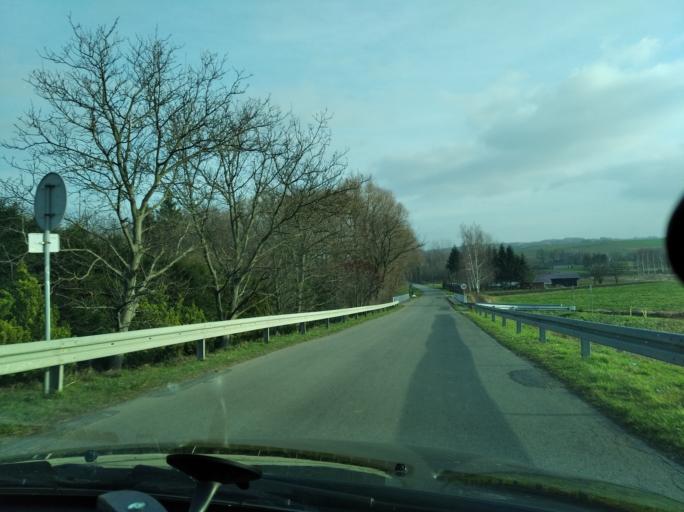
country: PL
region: Subcarpathian Voivodeship
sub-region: Powiat przeworski
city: Siedleczka
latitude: 49.9554
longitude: 22.3910
